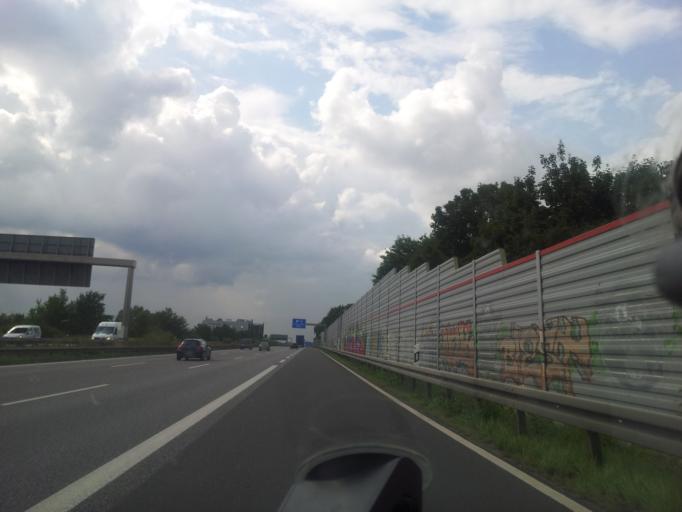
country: DE
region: Saxony
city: Rackwitz
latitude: 51.3998
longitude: 12.4145
